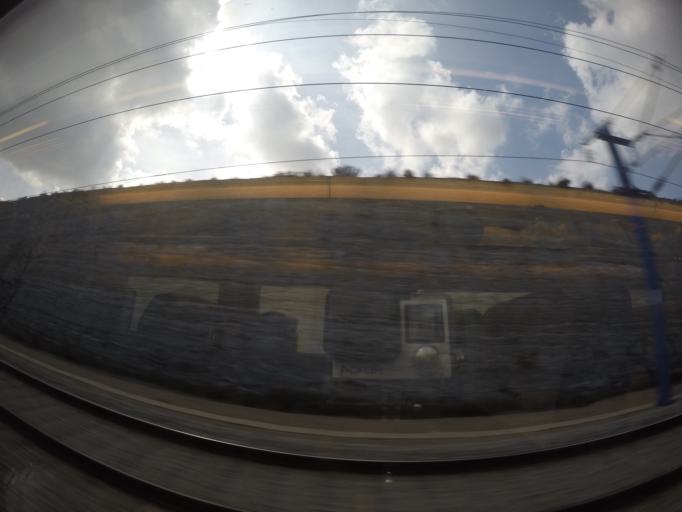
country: ES
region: Aragon
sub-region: Provincia de Zaragoza
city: El Burgo de Ebro
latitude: 41.5179
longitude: -0.6997
